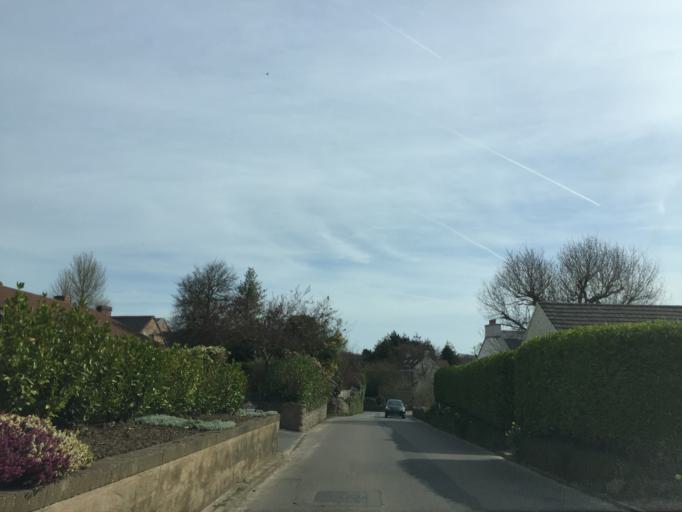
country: JE
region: St Helier
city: Saint Helier
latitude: 49.2323
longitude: -2.1019
